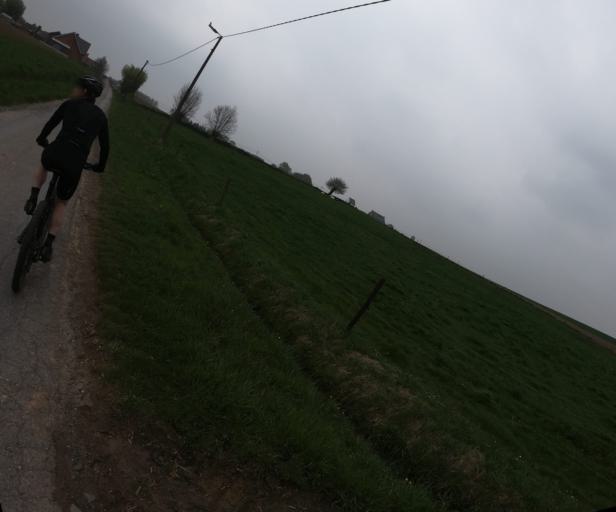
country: BE
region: Flanders
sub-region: Provincie Vlaams-Brabant
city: Pepingen
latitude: 50.7380
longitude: 4.1533
